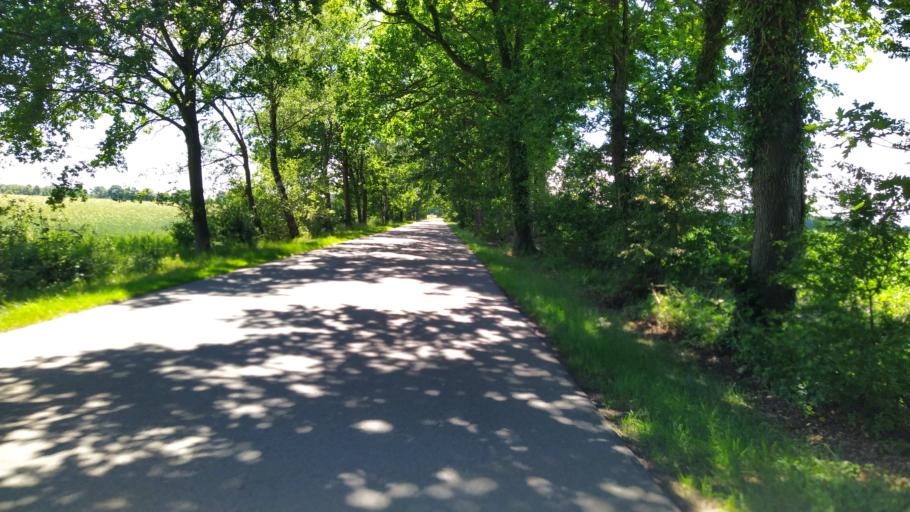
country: DE
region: Lower Saxony
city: Oldendorf
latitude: 53.5674
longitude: 9.2462
